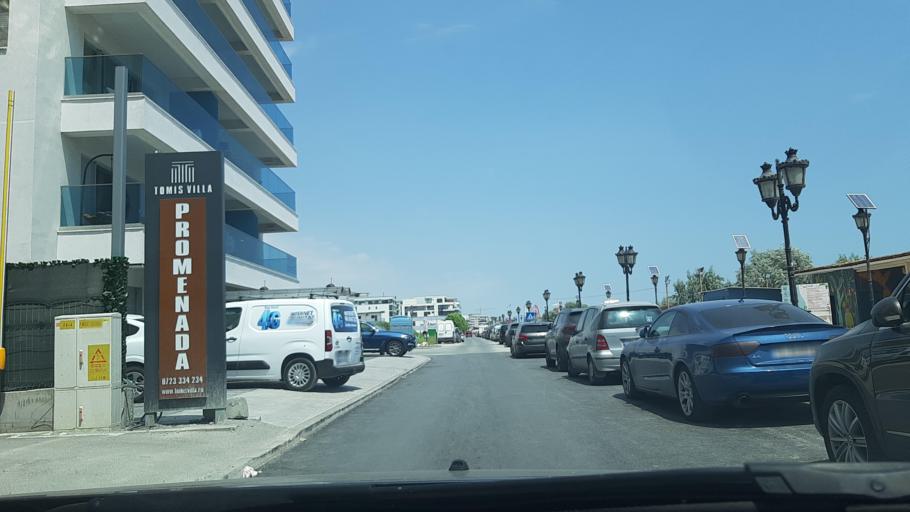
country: RO
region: Constanta
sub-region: Comuna Navodari
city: Navodari
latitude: 44.2945
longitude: 28.6243
